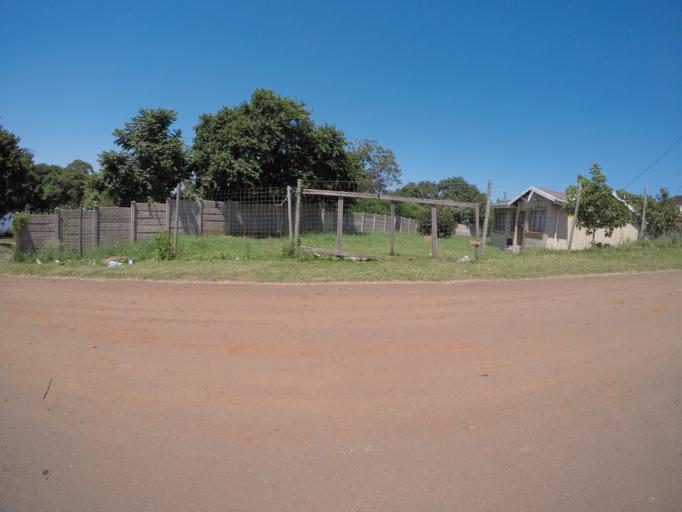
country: ZA
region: KwaZulu-Natal
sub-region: uThungulu District Municipality
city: Empangeni
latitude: -28.7713
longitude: 31.8835
